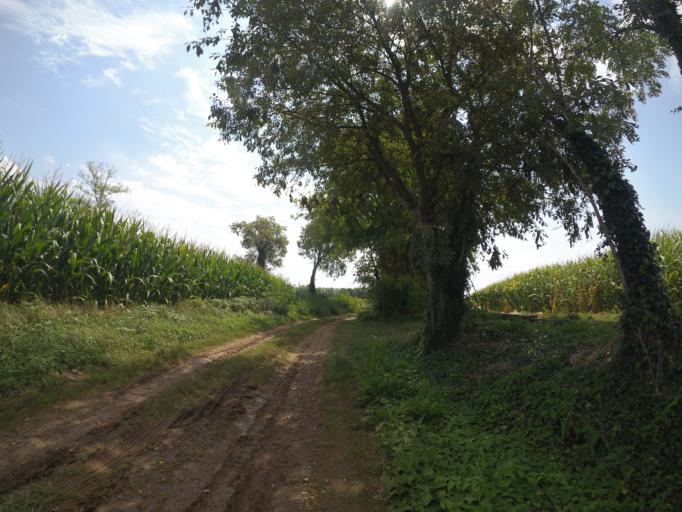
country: IT
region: Friuli Venezia Giulia
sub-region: Provincia di Udine
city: Bertiolo
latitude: 45.9605
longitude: 13.0693
